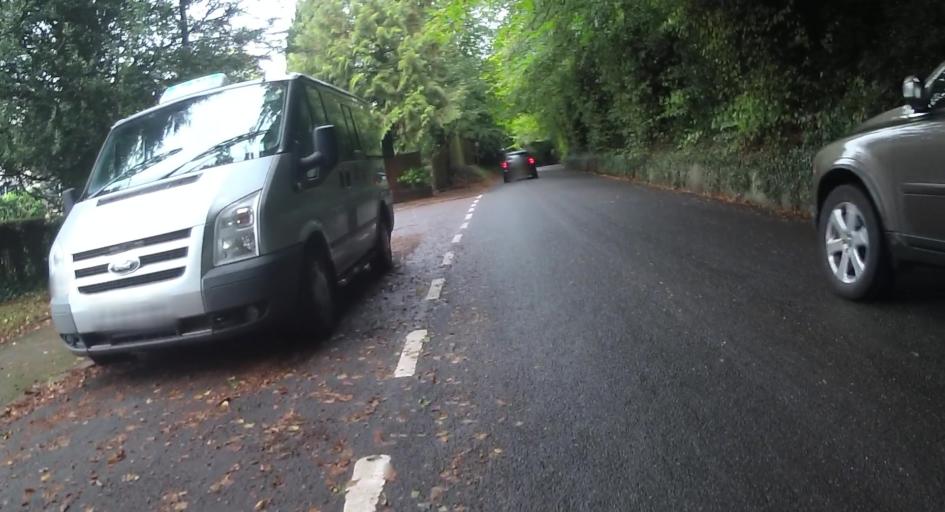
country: GB
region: England
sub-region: Hampshire
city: Tadley
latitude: 51.3992
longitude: -1.1774
